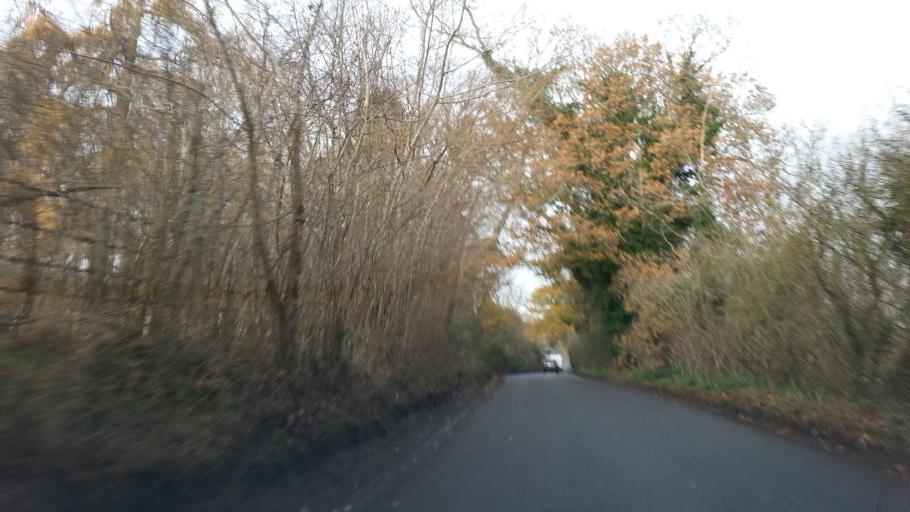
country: GB
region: England
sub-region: Suffolk
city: Wickham Market
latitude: 52.1525
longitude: 1.4111
